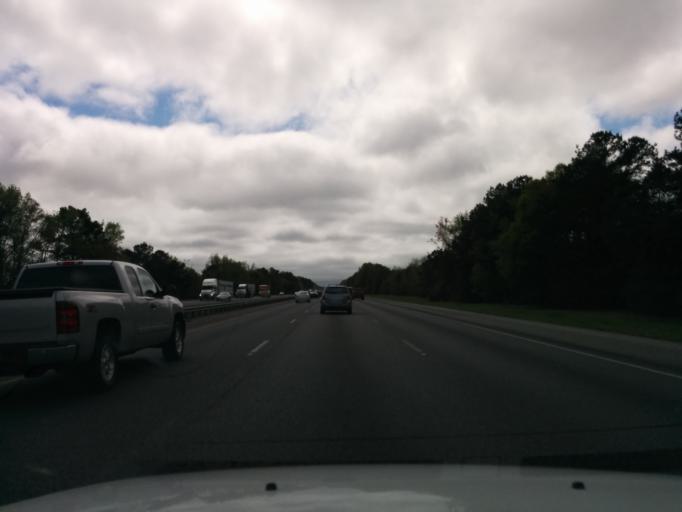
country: US
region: Georgia
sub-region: Chatham County
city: Georgetown
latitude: 32.0415
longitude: -81.2626
